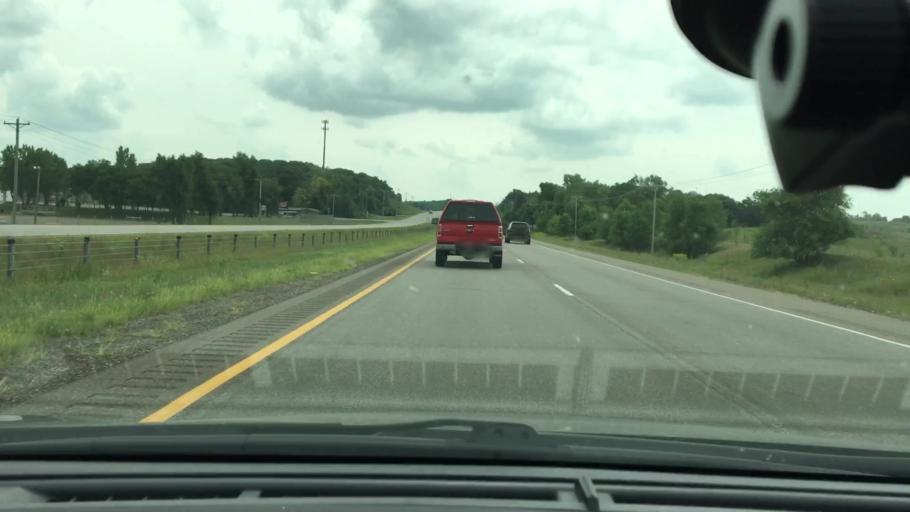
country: US
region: Minnesota
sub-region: Sherburne County
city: Elk River
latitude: 45.3653
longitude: -93.5644
